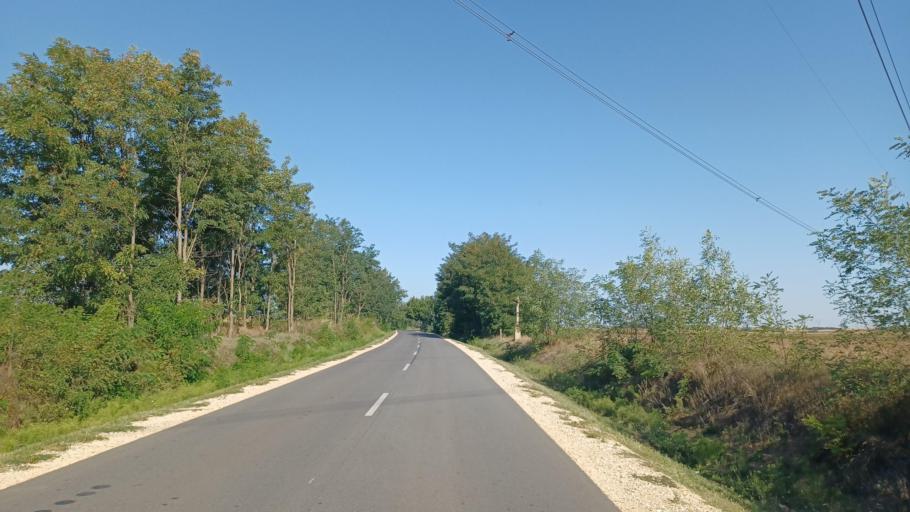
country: HU
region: Tolna
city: Nemetker
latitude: 46.6921
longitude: 18.7977
